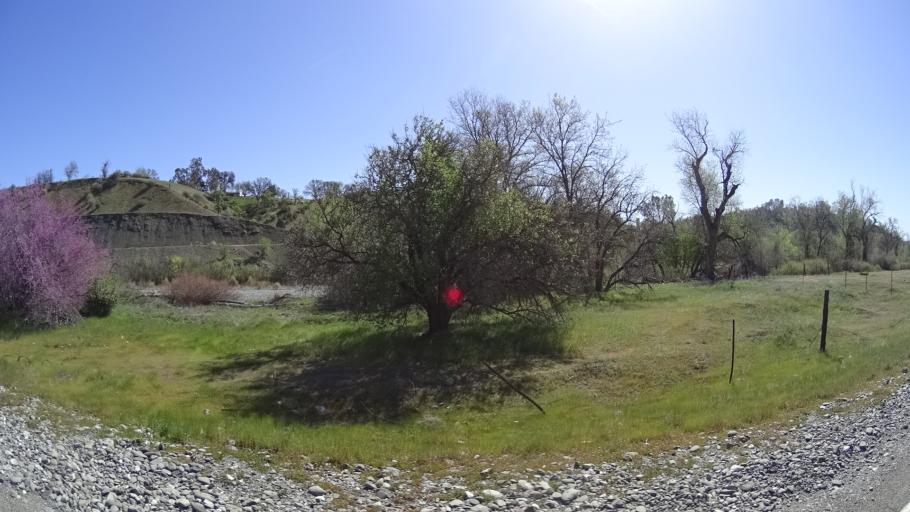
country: US
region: California
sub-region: Glenn County
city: Orland
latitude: 39.6761
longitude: -122.5255
